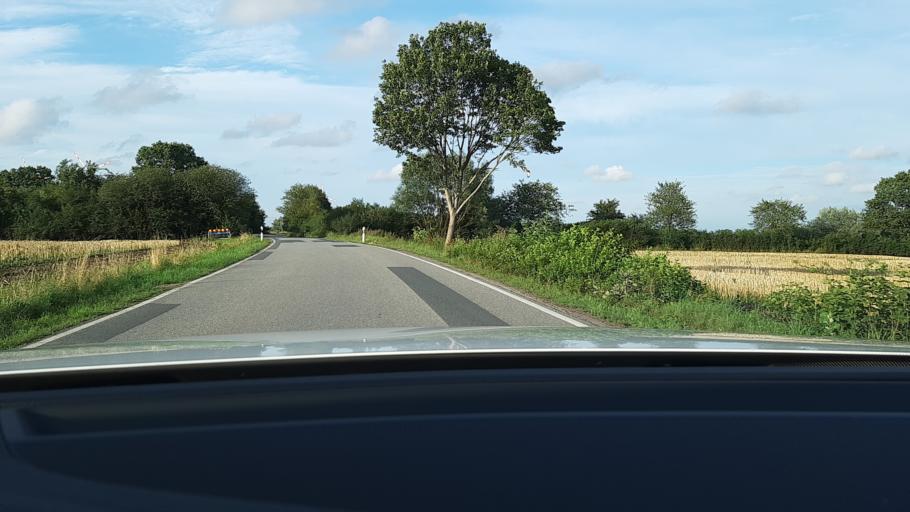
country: DE
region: Schleswig-Holstein
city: Monkhagen
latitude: 53.9217
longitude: 10.5594
